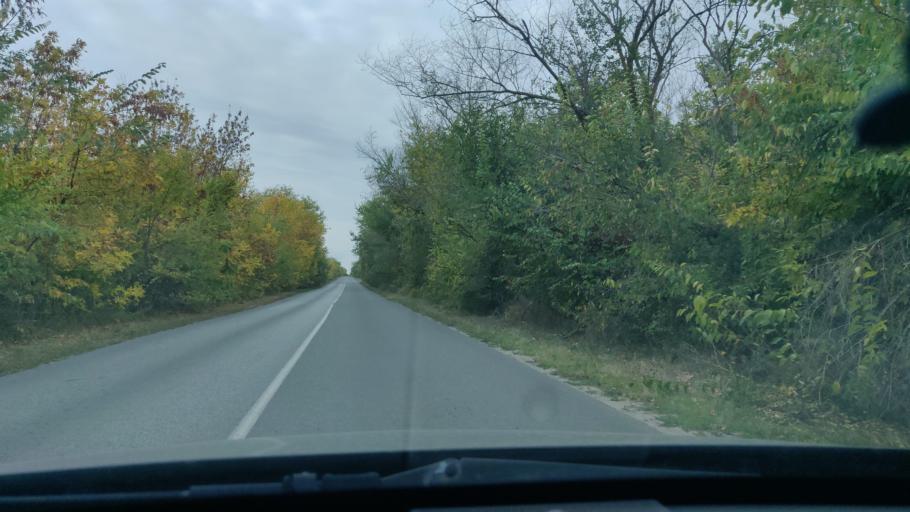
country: RU
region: Rostov
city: Ust'-Donetskiy
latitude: 47.6533
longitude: 40.8934
